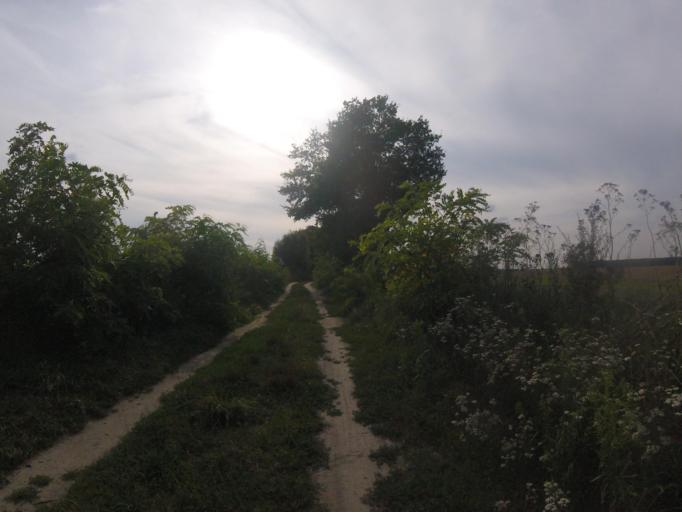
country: DE
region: Brandenburg
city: Mittenwalde
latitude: 52.2805
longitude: 13.5027
